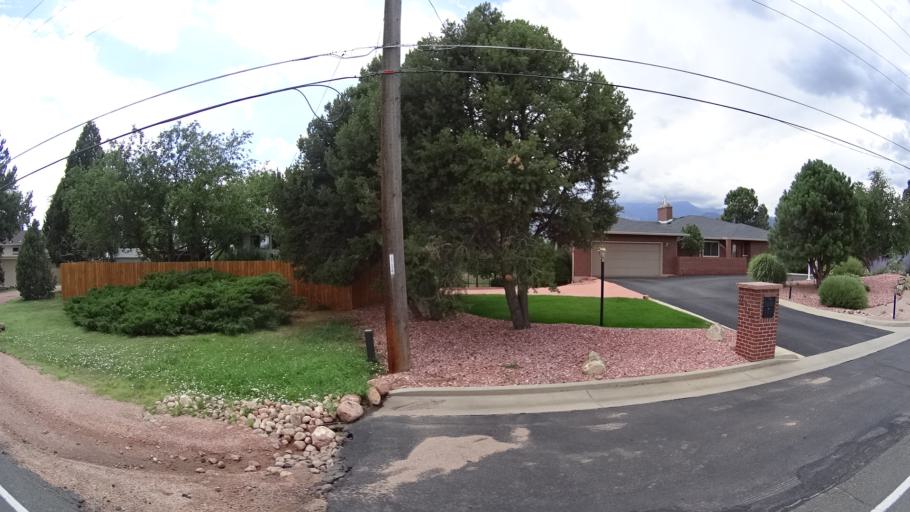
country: US
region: Colorado
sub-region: El Paso County
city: Colorado Springs
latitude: 38.8654
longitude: -104.8554
